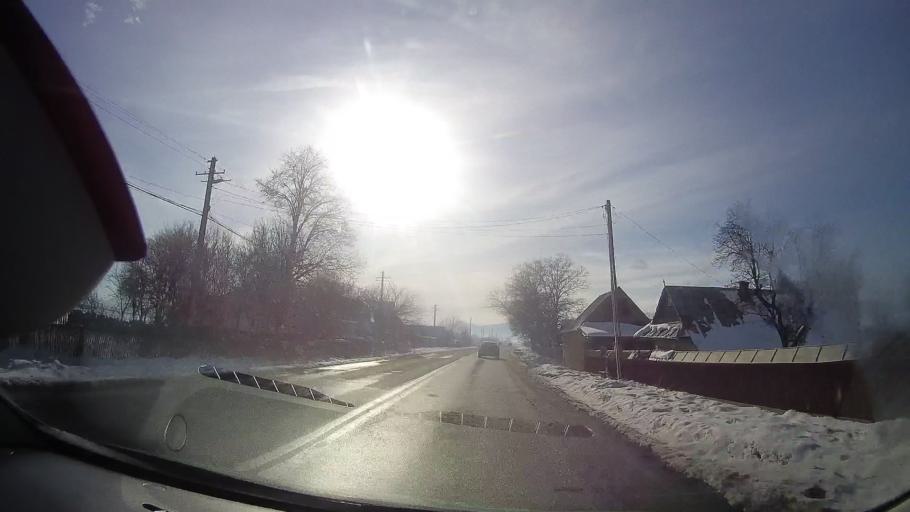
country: RO
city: Vanatori-Neamt
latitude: 47.1800
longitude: 26.3300
